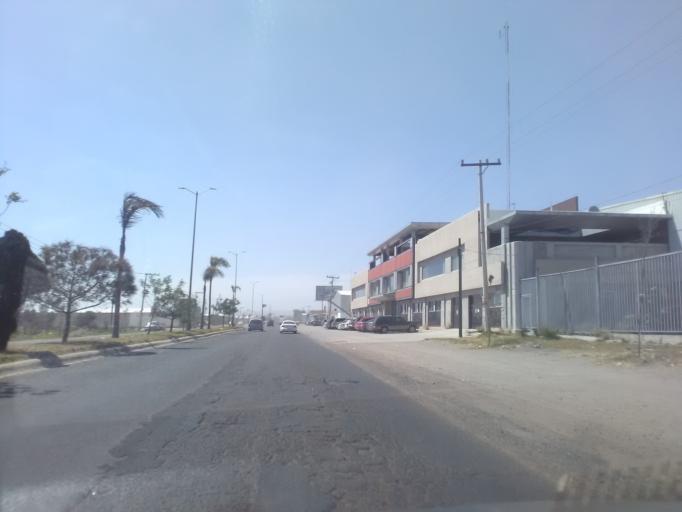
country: MX
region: Durango
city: Victoria de Durango
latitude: 24.0296
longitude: -104.6045
